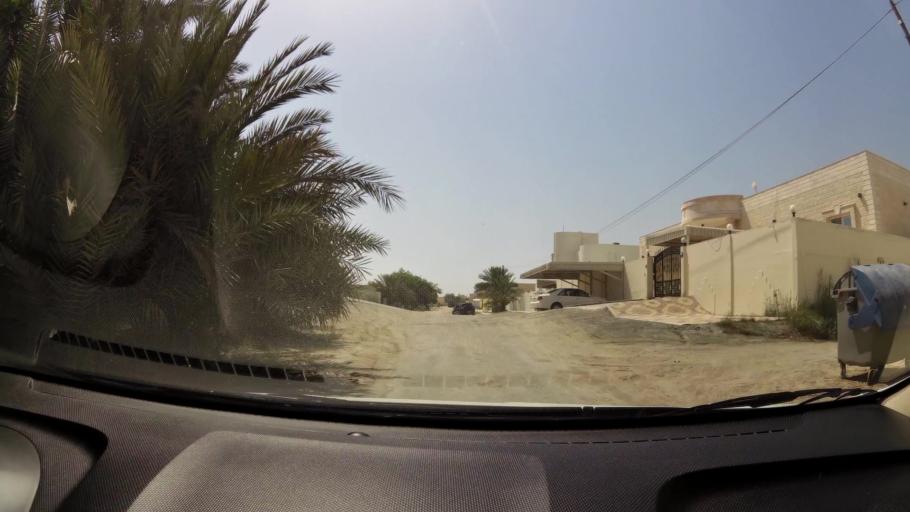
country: AE
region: Ajman
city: Ajman
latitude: 25.4134
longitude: 55.4797
